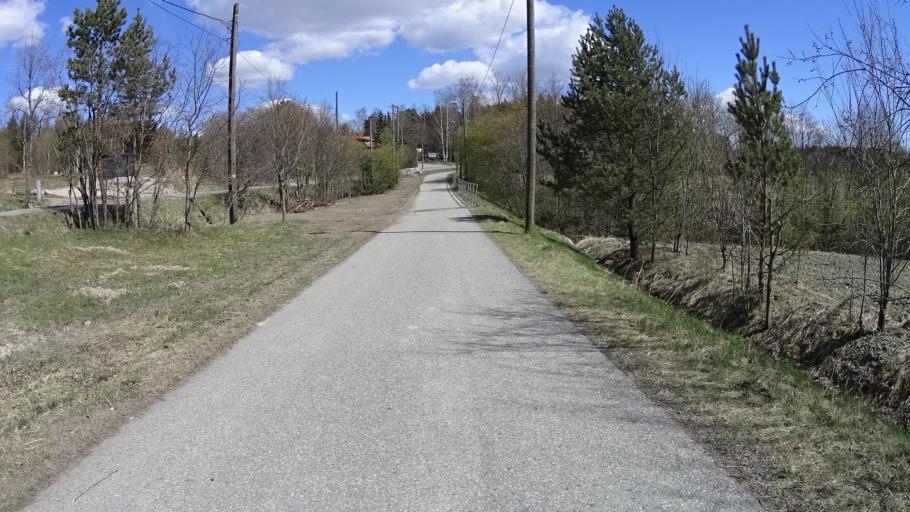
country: FI
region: Uusimaa
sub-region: Helsinki
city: Espoo
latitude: 60.2244
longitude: 24.6789
